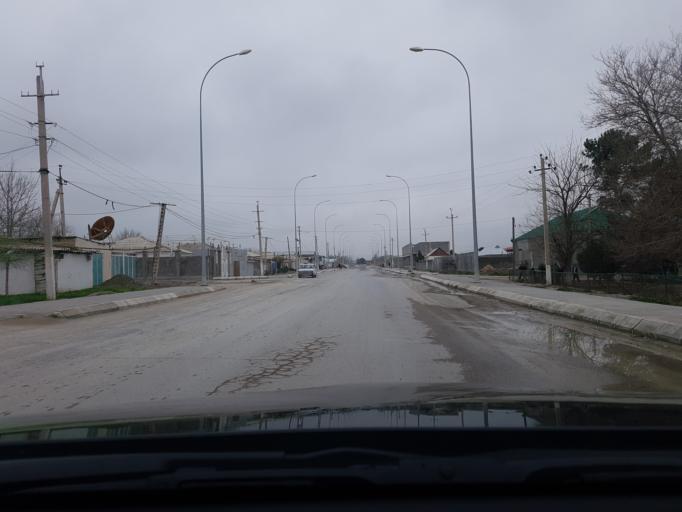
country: TM
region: Ahal
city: Abadan
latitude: 38.1544
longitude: 57.9568
